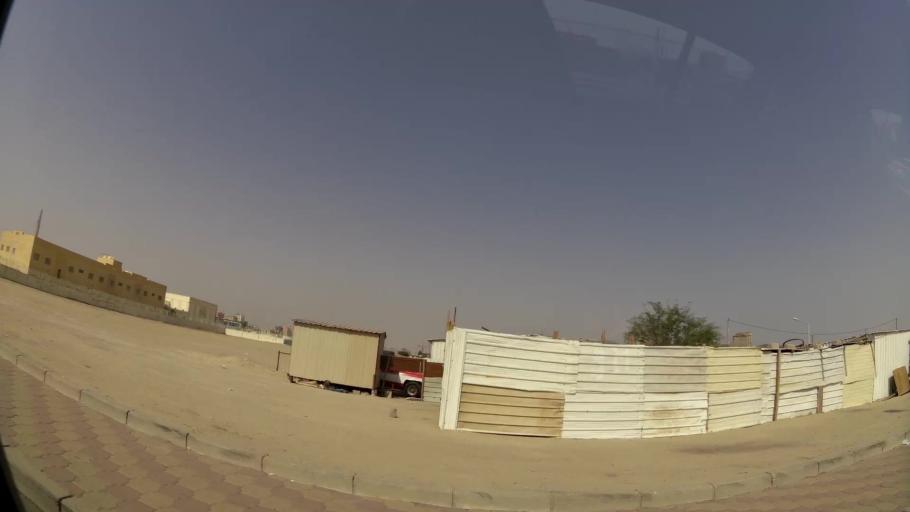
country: KW
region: Muhafazat al Jahra'
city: Al Jahra'
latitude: 29.3298
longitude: 47.6774
